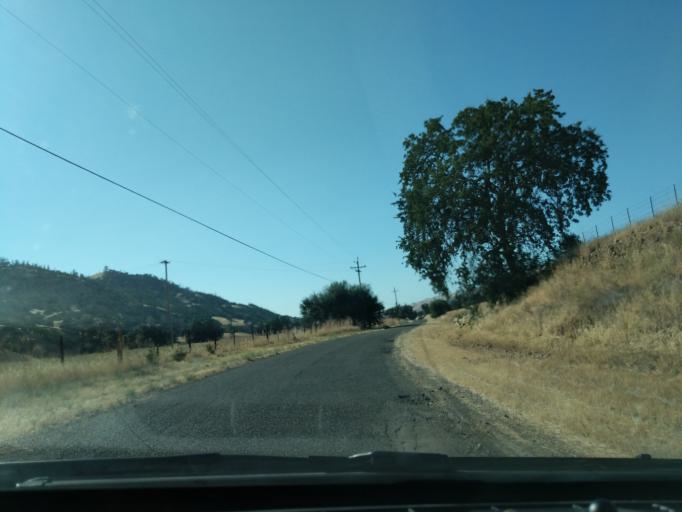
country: US
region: California
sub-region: San Luis Obispo County
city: San Miguel
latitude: 36.1298
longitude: -120.7435
